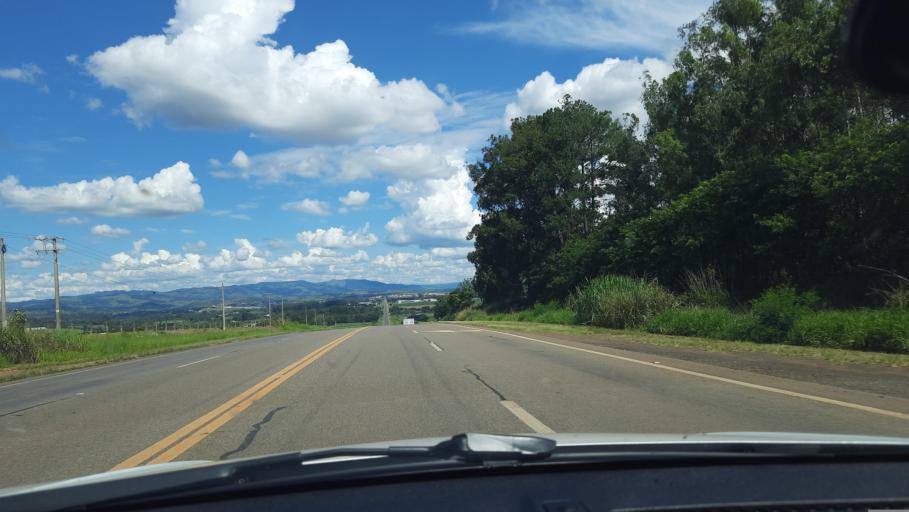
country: BR
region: Sao Paulo
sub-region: Vargem Grande Do Sul
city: Vargem Grande do Sul
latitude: -21.8189
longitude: -46.9721
